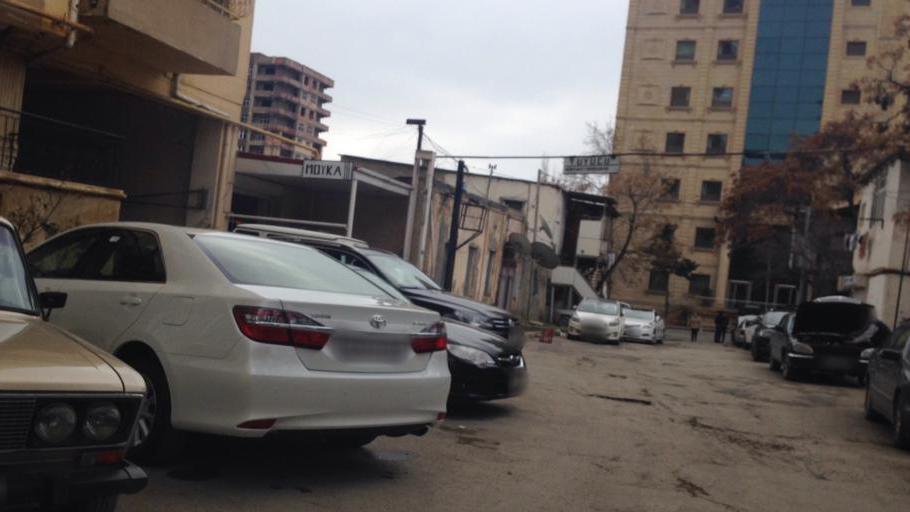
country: AZ
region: Baki
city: Badamdar
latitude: 40.3814
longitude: 49.8254
